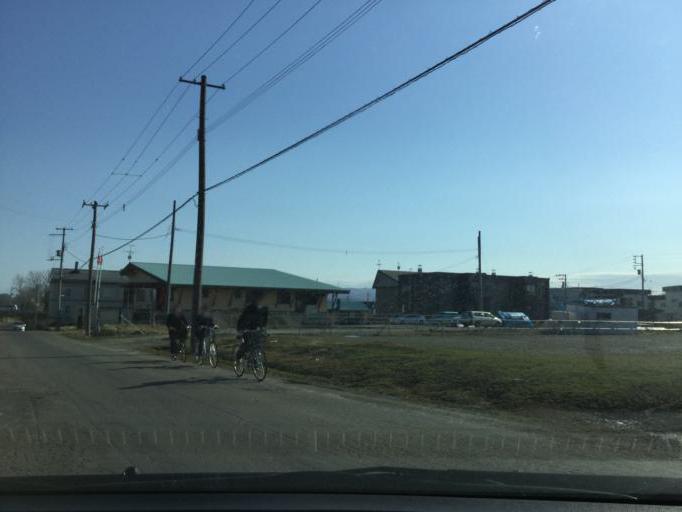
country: JP
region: Hokkaido
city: Iwamizawa
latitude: 43.2183
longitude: 141.7872
